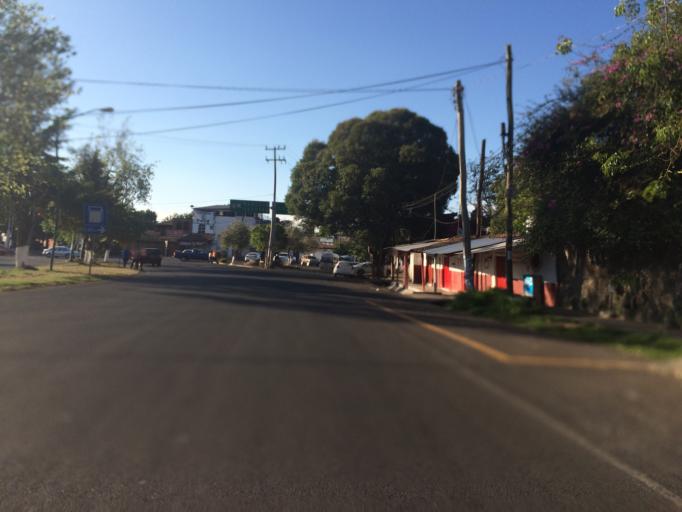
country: MX
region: Michoacan
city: Patzcuaro
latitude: 19.5078
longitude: -101.6132
